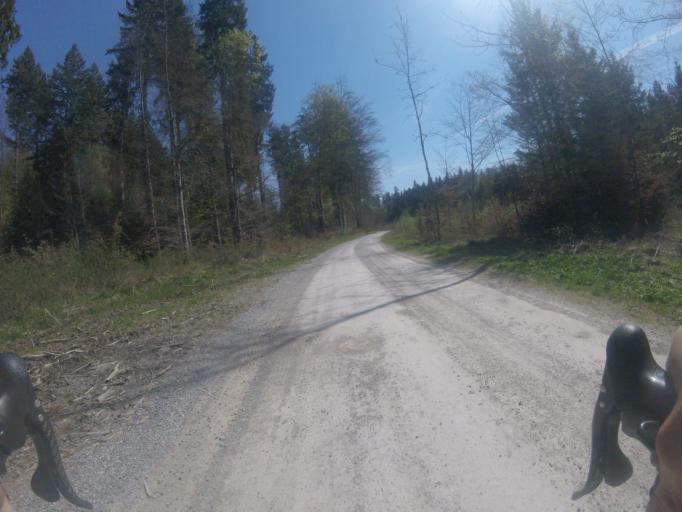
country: CH
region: Fribourg
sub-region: Sense District
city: Flamatt
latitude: 46.9142
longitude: 7.3236
